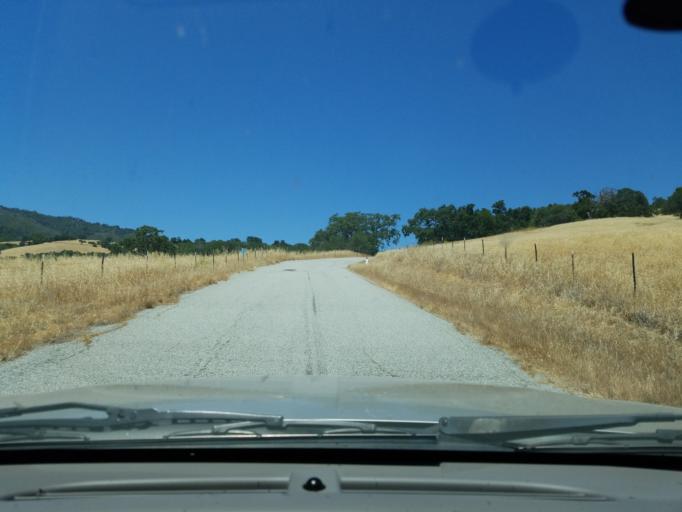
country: US
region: California
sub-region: Monterey County
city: Gonzales
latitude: 36.3402
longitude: -121.5136
